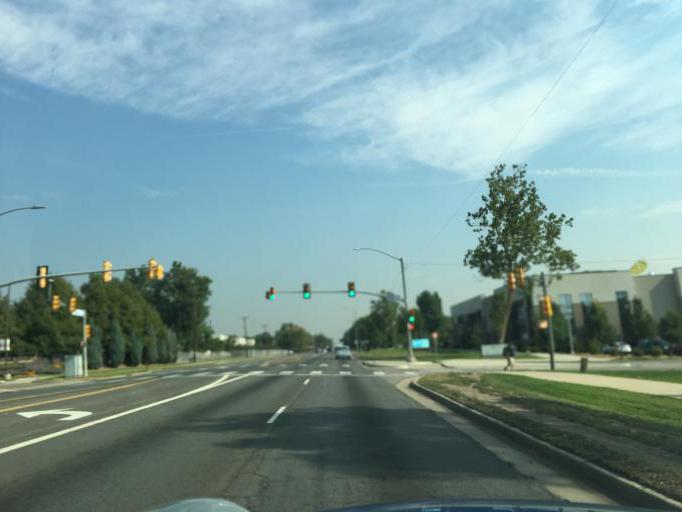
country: US
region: Colorado
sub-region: Jefferson County
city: Wheat Ridge
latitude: 39.7579
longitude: -105.0814
